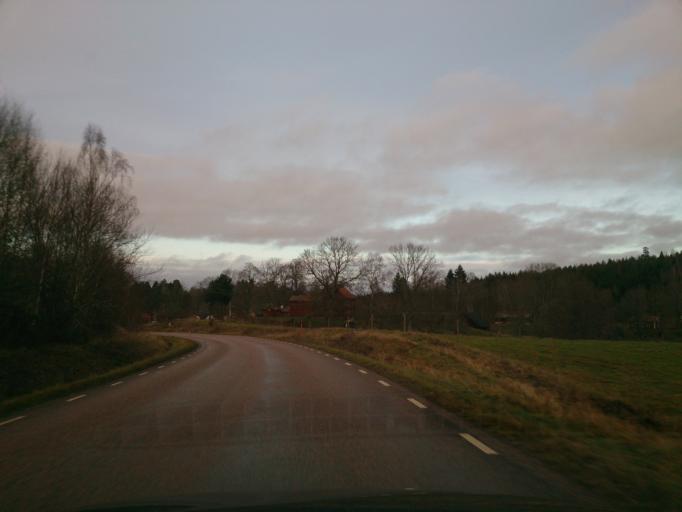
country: SE
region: OEstergoetland
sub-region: Atvidabergs Kommun
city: Atvidaberg
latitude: 58.3328
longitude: 16.0285
